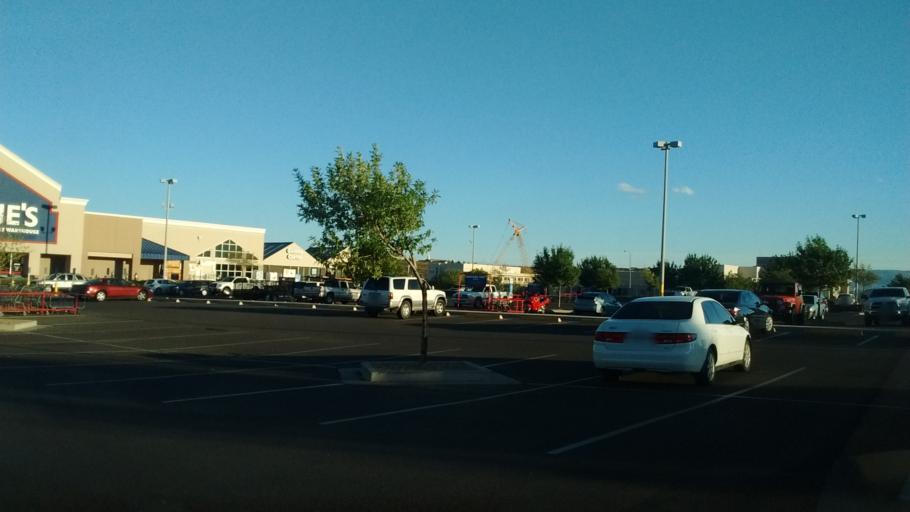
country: US
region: Utah
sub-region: Washington County
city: Saint George
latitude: 37.1012
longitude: -113.5550
